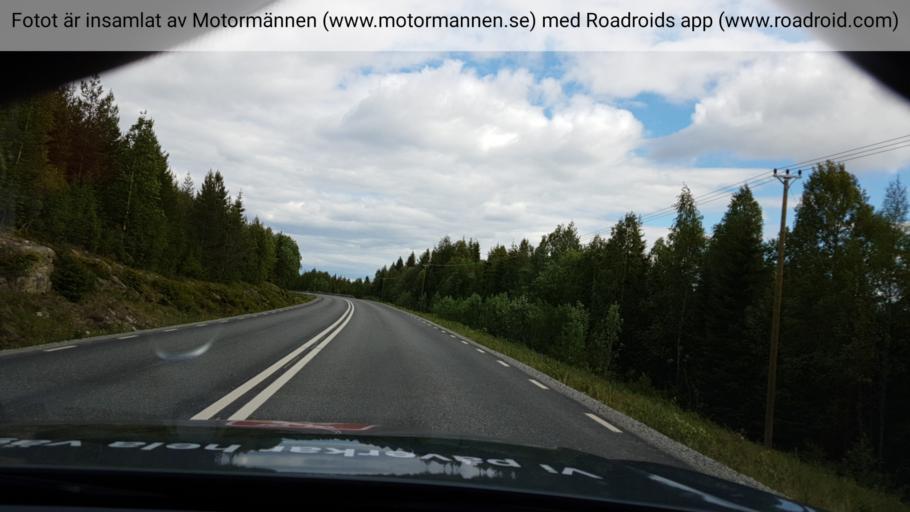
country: SE
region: Jaemtland
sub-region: Stroemsunds Kommun
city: Stroemsund
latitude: 64.1992
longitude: 15.6036
